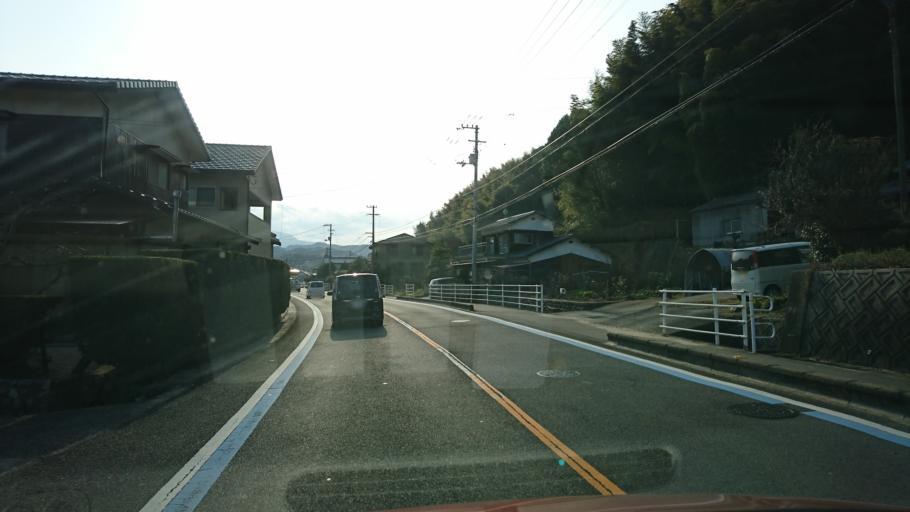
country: JP
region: Ehime
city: Hojo
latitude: 34.0256
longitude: 132.9469
